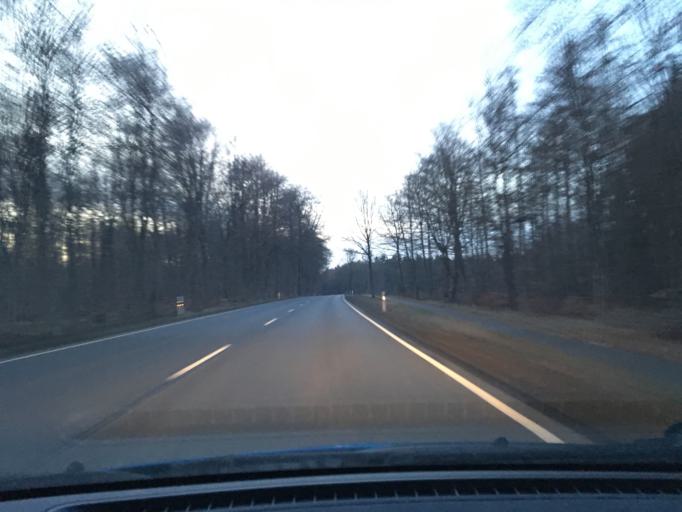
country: DE
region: Lower Saxony
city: Reinstorf
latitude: 53.2236
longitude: 10.5566
